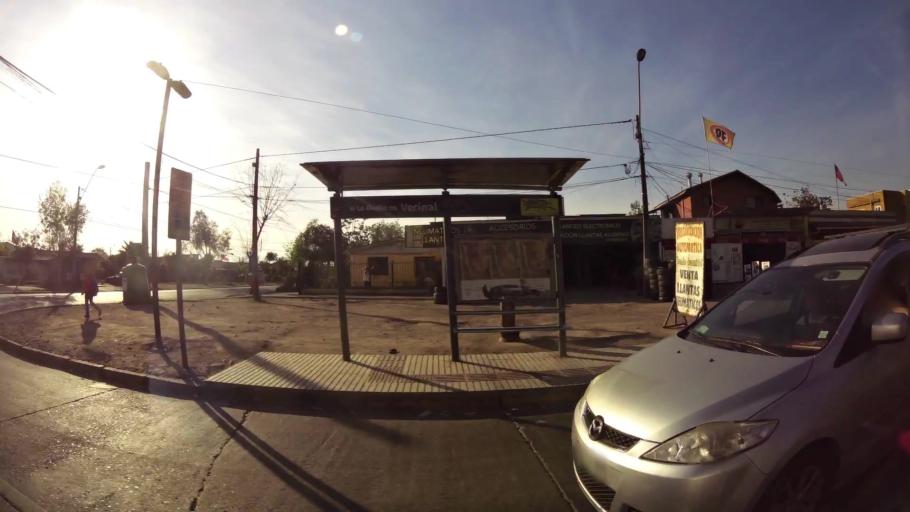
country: CL
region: Santiago Metropolitan
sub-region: Provincia de Santiago
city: Santiago
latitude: -33.5146
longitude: -70.6207
